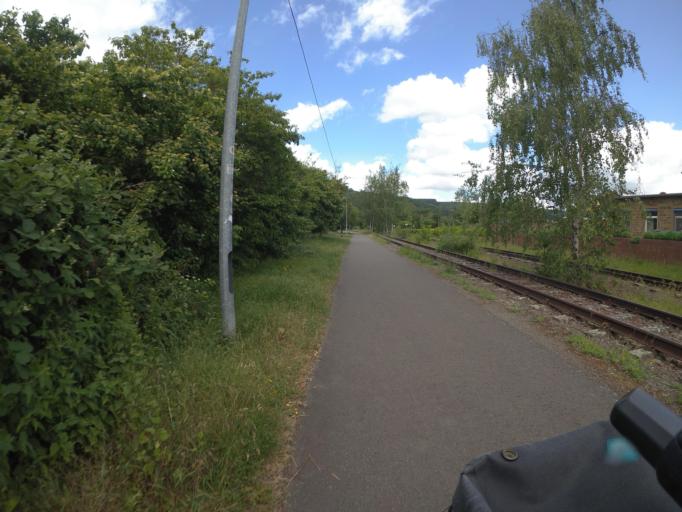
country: DE
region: Rheinland-Pfalz
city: Meisenheim
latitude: 49.7118
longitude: 7.6626
